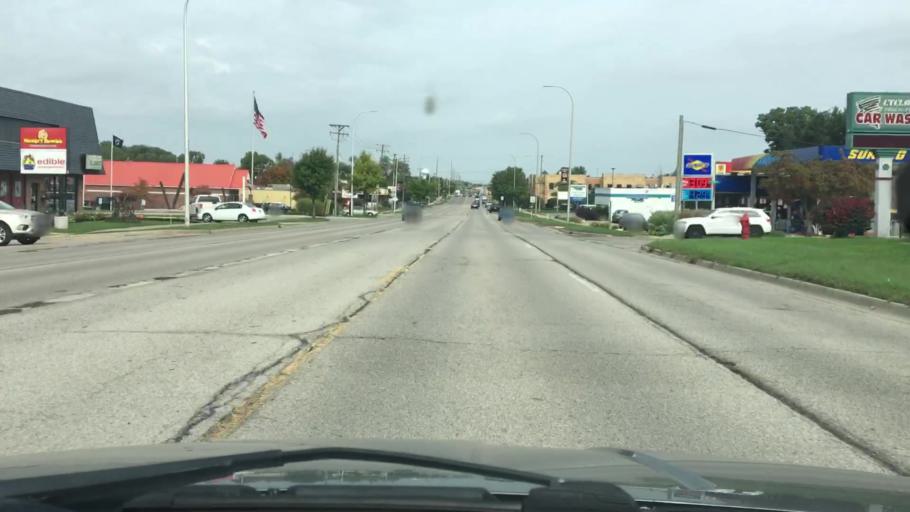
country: US
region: Michigan
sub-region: Livingston County
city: Brighton
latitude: 42.5334
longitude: -83.7824
